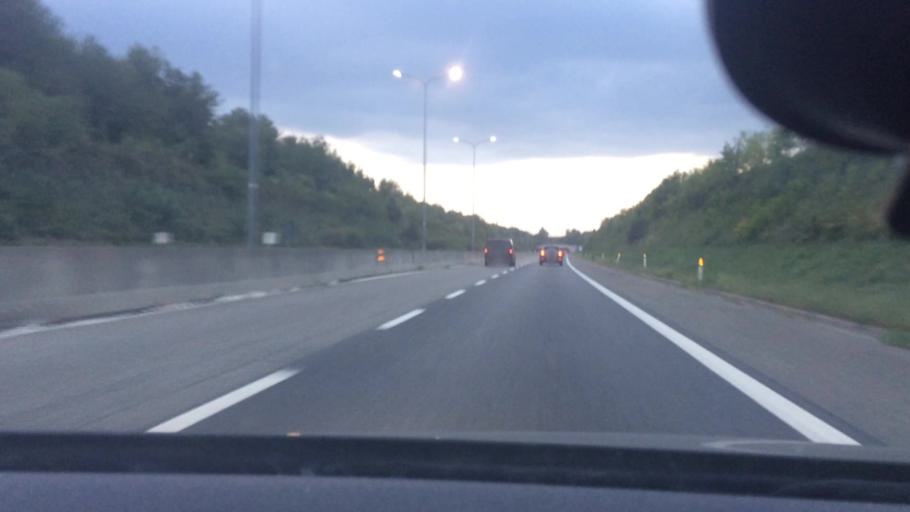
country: IT
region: Lombardy
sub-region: Provincia di Varese
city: Vizzola Ticino
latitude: 45.5994
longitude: 8.7131
